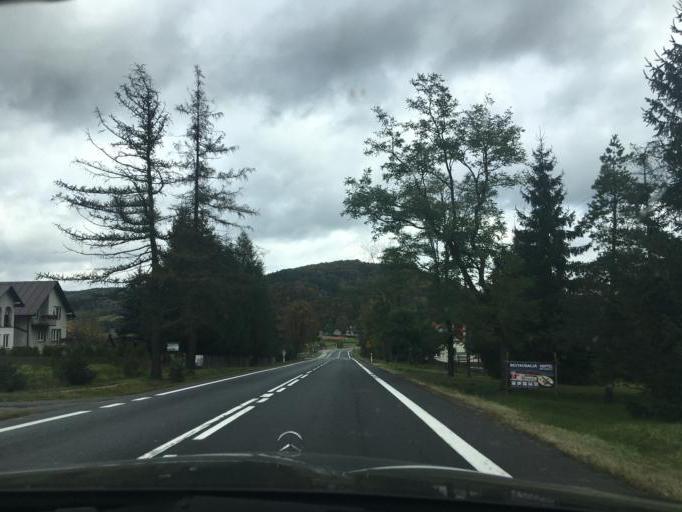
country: PL
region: Subcarpathian Voivodeship
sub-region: Powiat krosnienski
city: Dukla
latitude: 49.4602
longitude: 21.6943
